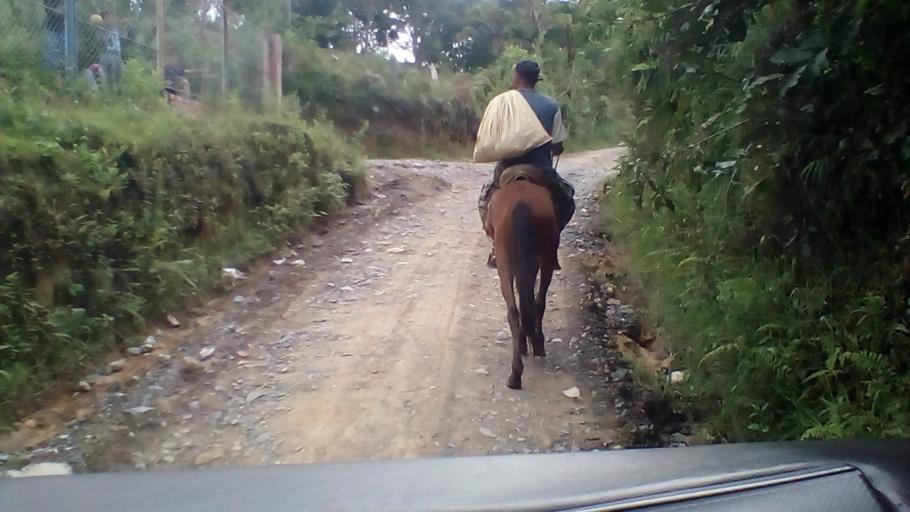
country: CO
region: Boyaca
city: Santana
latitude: 6.0020
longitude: -73.5069
